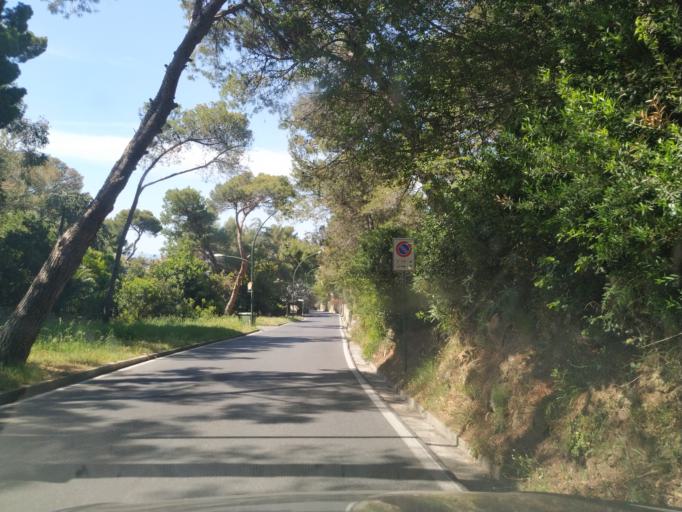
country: IT
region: Liguria
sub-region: Provincia di Savona
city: Marina di Andora
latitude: 43.9551
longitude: 8.1602
